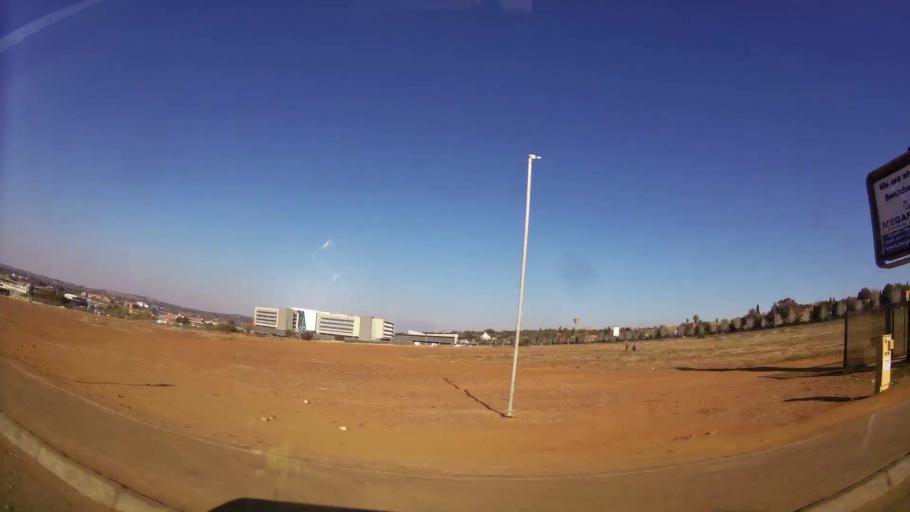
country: ZA
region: Gauteng
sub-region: City of Tshwane Metropolitan Municipality
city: Centurion
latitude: -25.8583
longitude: 28.1814
